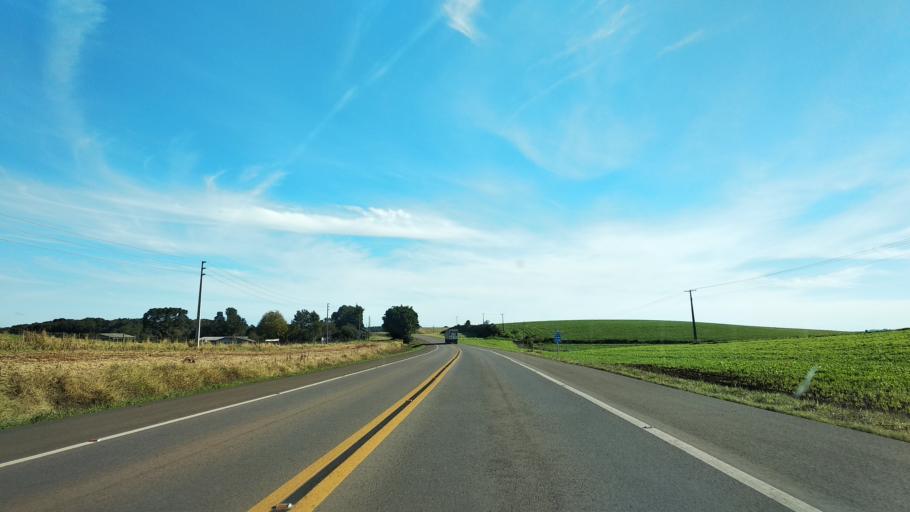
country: BR
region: Santa Catarina
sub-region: Campos Novos
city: Campos Novos
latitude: -27.4925
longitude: -51.3339
